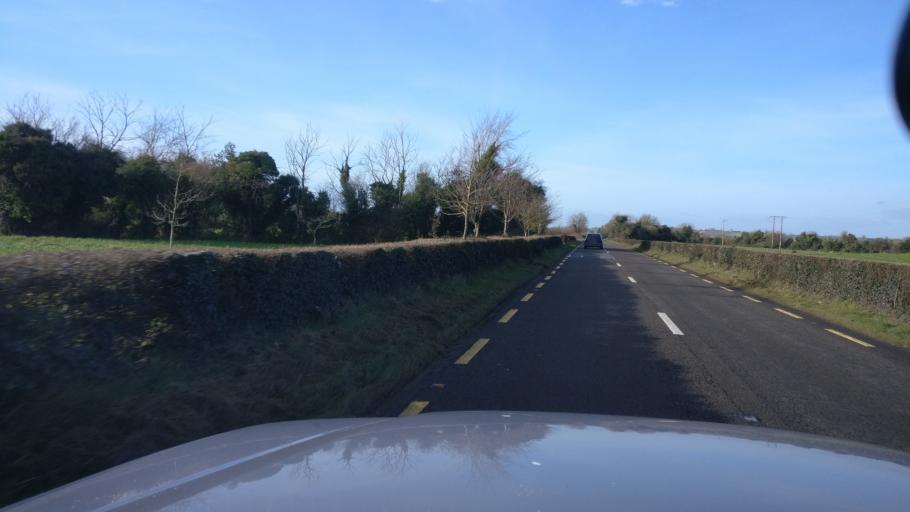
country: IE
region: Leinster
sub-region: Laois
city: Mountmellick
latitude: 53.1723
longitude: -7.3830
